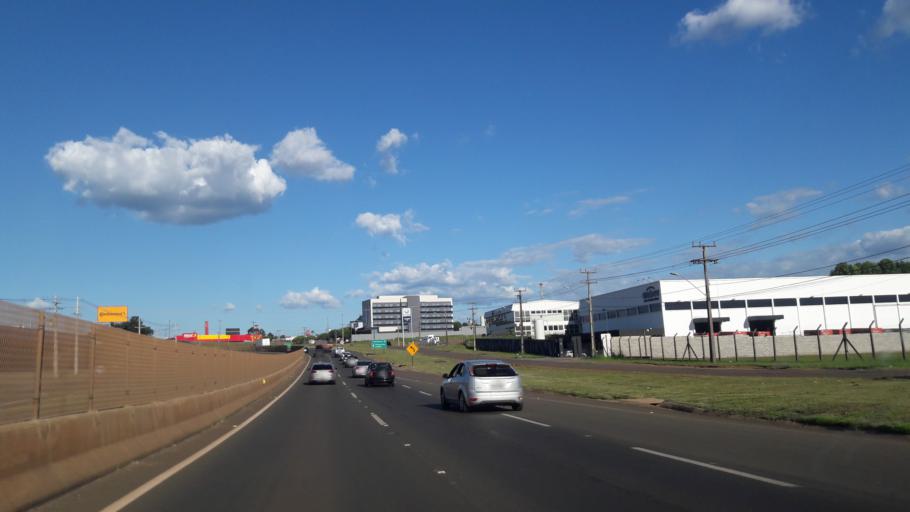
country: BR
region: Parana
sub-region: Guarapuava
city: Guarapuava
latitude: -25.3658
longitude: -51.4809
